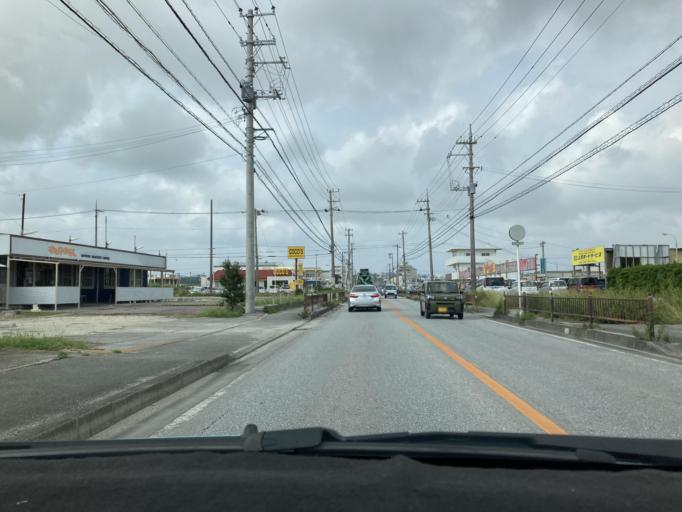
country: JP
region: Okinawa
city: Tomigusuku
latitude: 26.1667
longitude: 127.6680
